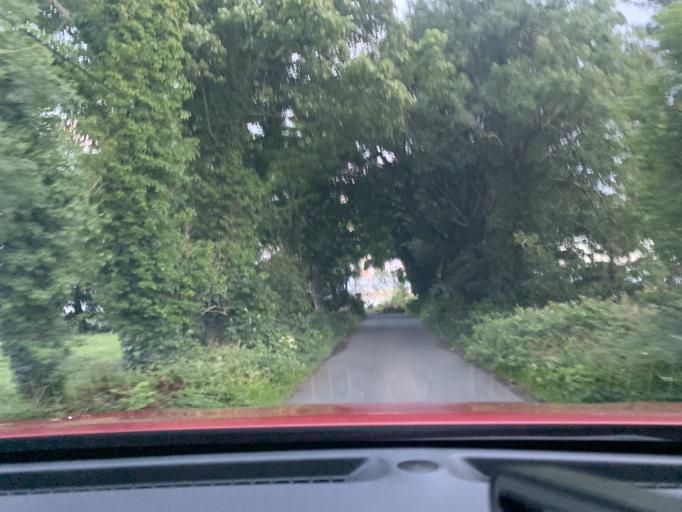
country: IE
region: Connaught
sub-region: Sligo
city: Sligo
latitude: 54.3444
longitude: -8.4903
